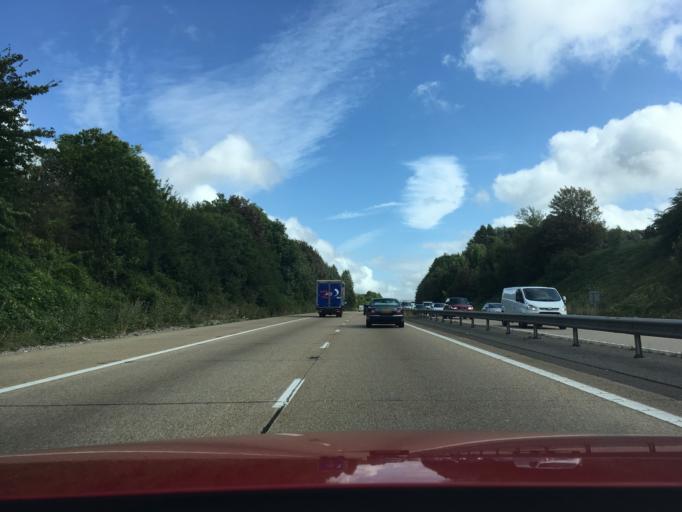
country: GB
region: England
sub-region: Hampshire
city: Overton
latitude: 51.1890
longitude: -1.2086
